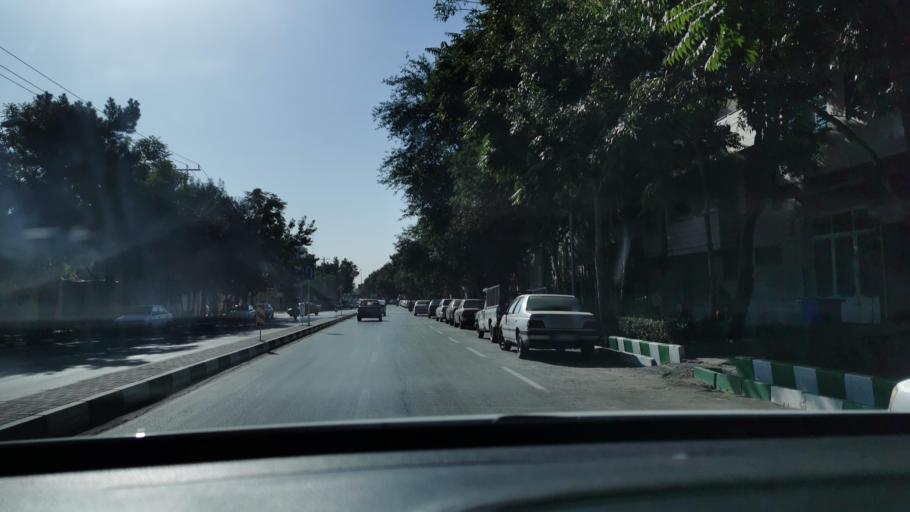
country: IR
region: Razavi Khorasan
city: Mashhad
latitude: 36.2974
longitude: 59.6217
